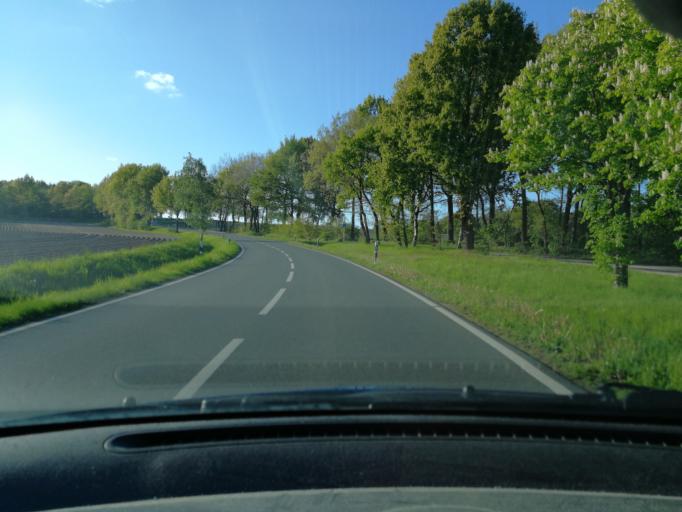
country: DE
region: Lower Saxony
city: Betzendorf
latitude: 53.1250
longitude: 10.3104
